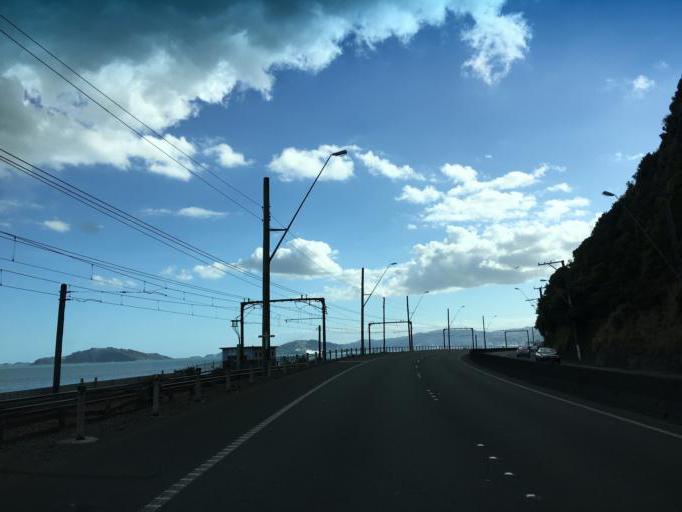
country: NZ
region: Wellington
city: Petone
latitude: -41.2302
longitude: 174.8418
